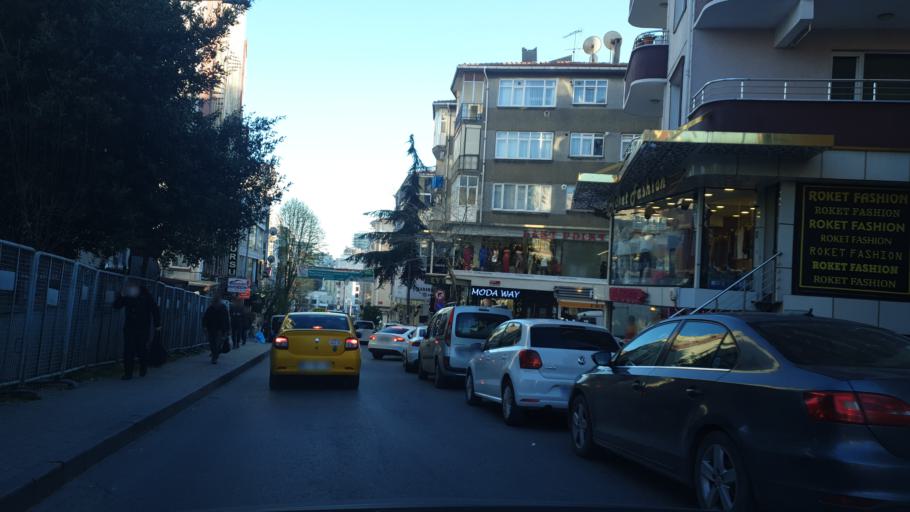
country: TR
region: Istanbul
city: merter keresteciler
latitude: 41.0178
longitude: 28.8759
